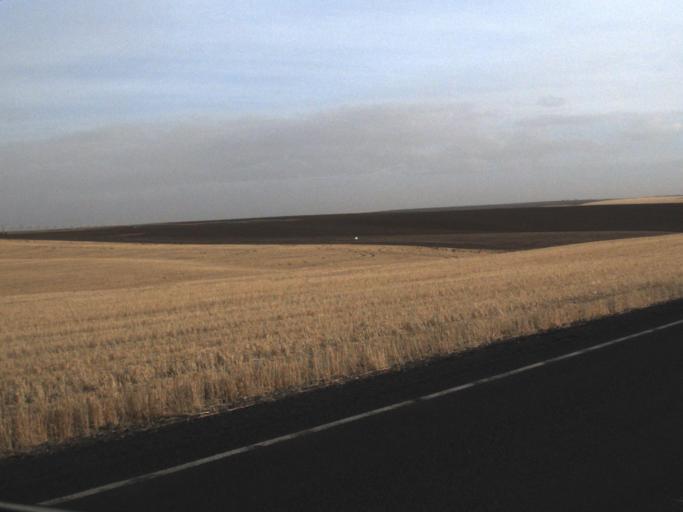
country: US
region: Washington
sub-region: Adams County
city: Ritzville
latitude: 47.1942
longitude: -118.6868
